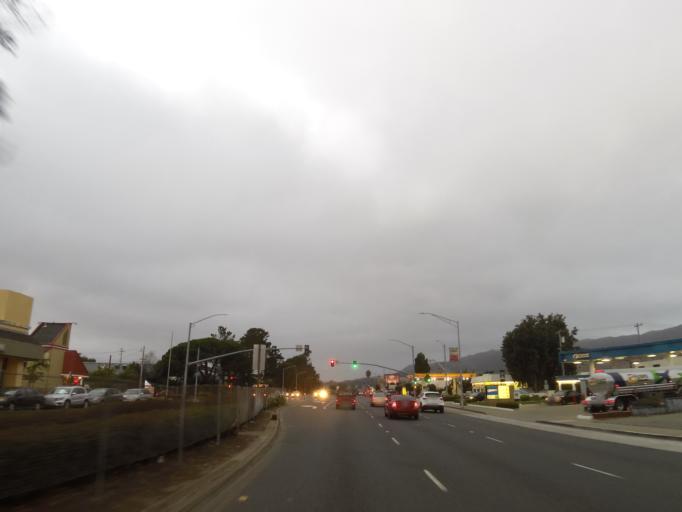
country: US
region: California
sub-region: San Mateo County
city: South San Francisco
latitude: 37.6495
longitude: -122.4301
